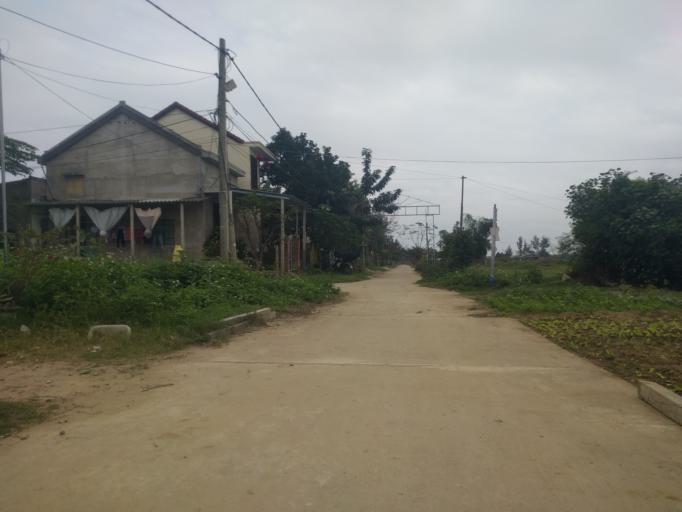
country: VN
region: Quang Nam
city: Hoi An
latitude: 15.8664
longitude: 108.3522
